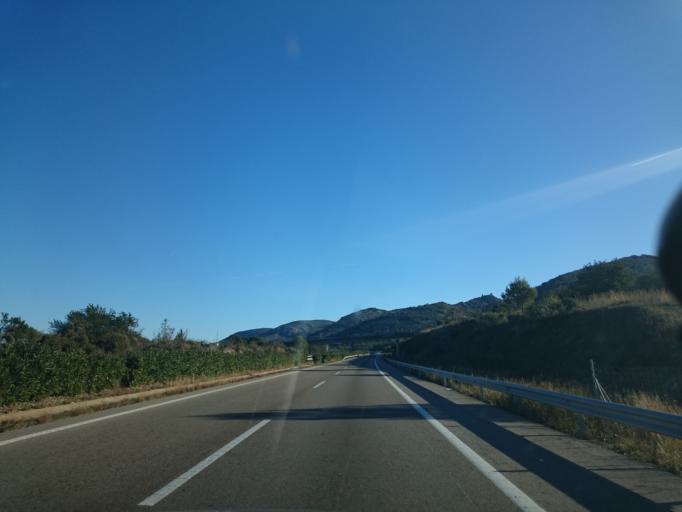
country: ES
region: Valencia
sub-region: Provincia de Castello
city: Santa Magdalena de Pulpis
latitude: 40.3516
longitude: 0.3016
